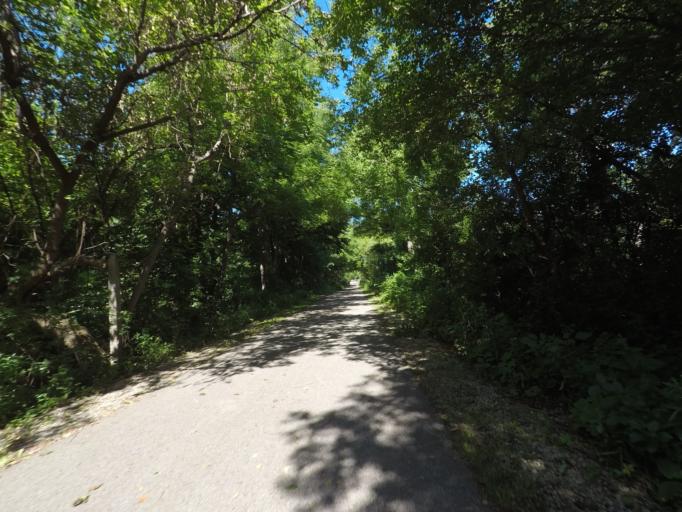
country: US
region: Wisconsin
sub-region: Milwaukee County
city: West Milwaukee
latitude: 43.0251
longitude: -87.9720
